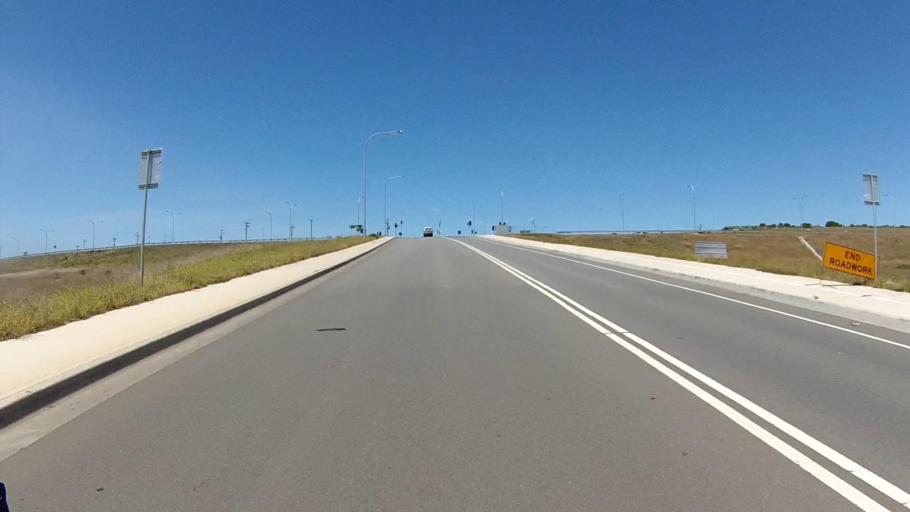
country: AU
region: Tasmania
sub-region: Clarence
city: Howrah
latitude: -42.8876
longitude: 147.4286
